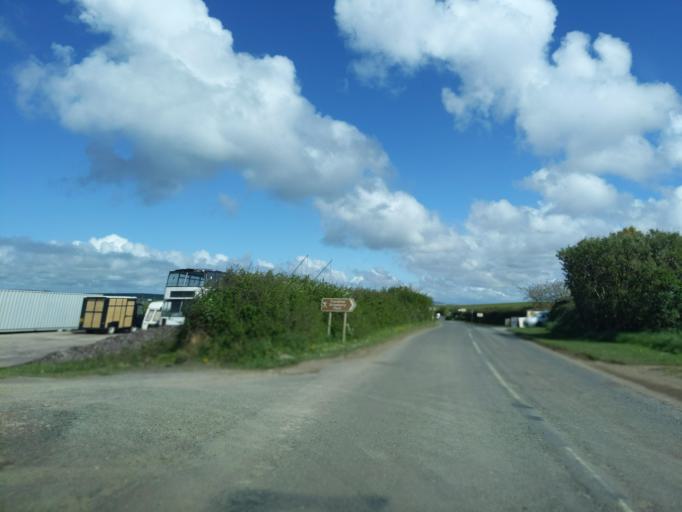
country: GB
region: England
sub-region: Cornwall
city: Wadebridge
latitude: 50.5734
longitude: -4.8284
